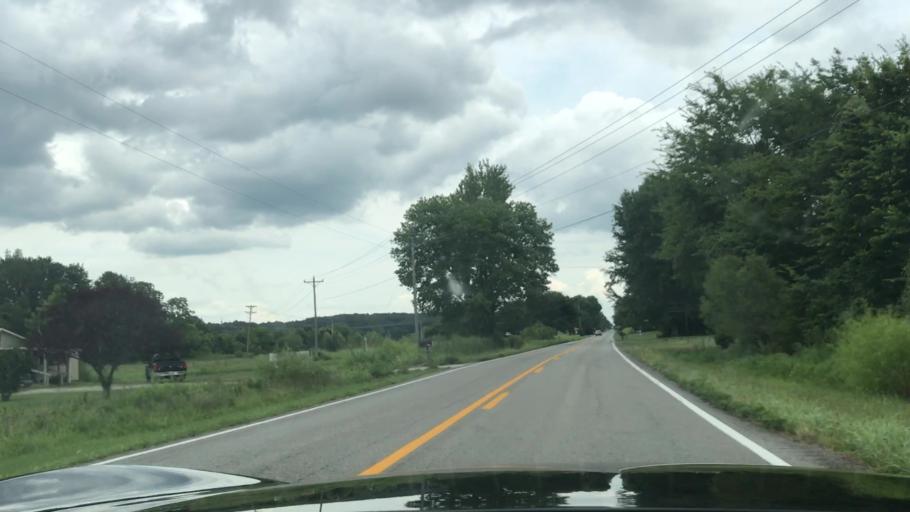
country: US
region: Kentucky
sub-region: Muhlenberg County
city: Central City
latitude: 37.2037
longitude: -87.0133
